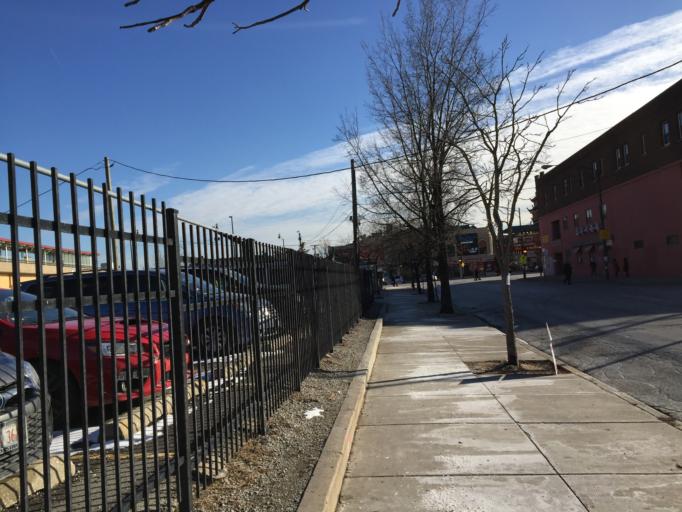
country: US
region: Illinois
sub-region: Cook County
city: Chicago
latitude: 41.8538
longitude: -87.6317
